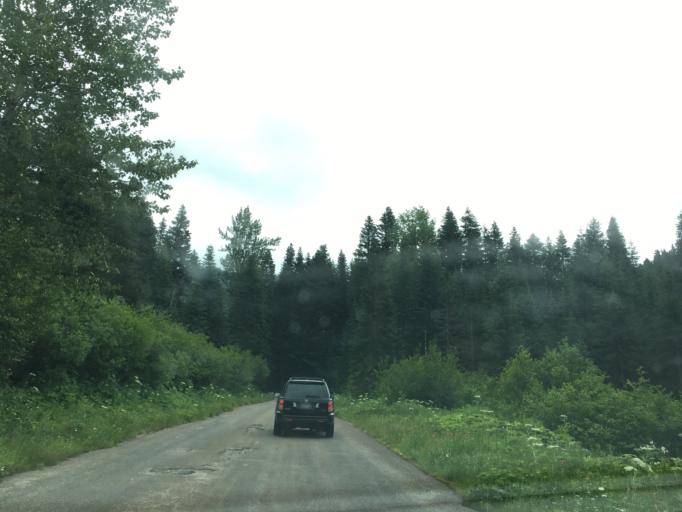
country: US
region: Washington
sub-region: Chelan County
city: Leavenworth
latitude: 47.7498
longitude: -121.1015
